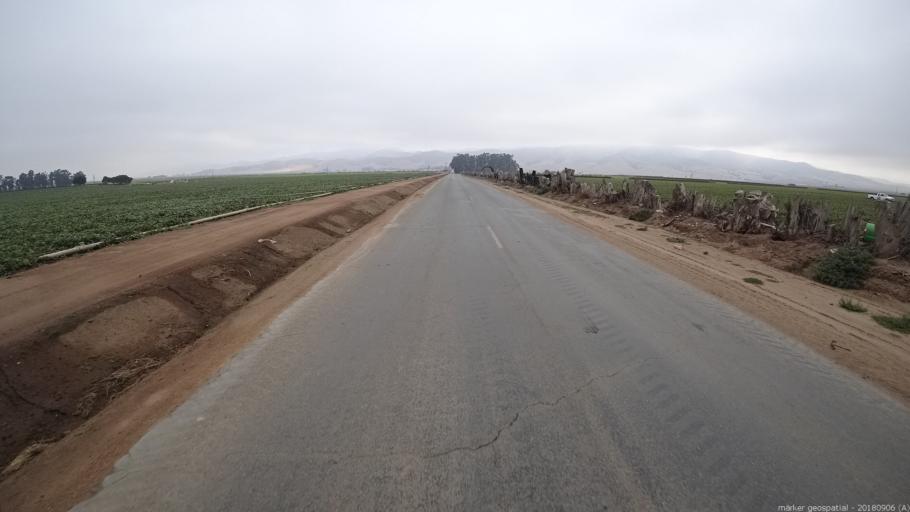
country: US
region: California
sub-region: Monterey County
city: Chualar
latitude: 36.6475
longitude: -121.5650
